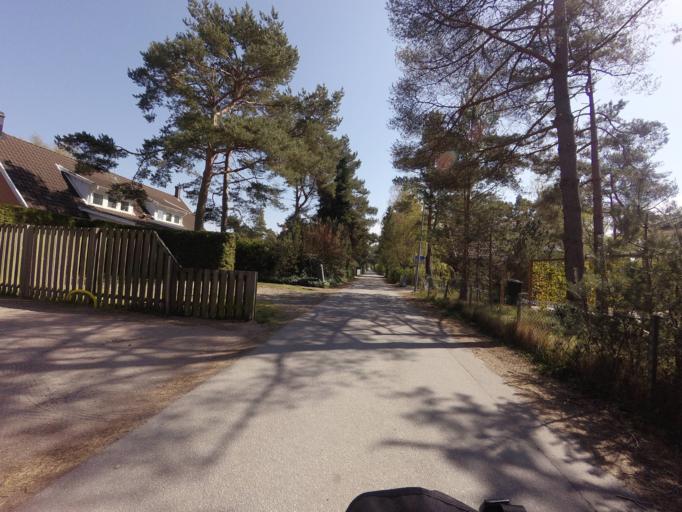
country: SE
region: Skane
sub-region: Vellinge Kommun
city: Hollviken
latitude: 55.4069
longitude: 12.9506
